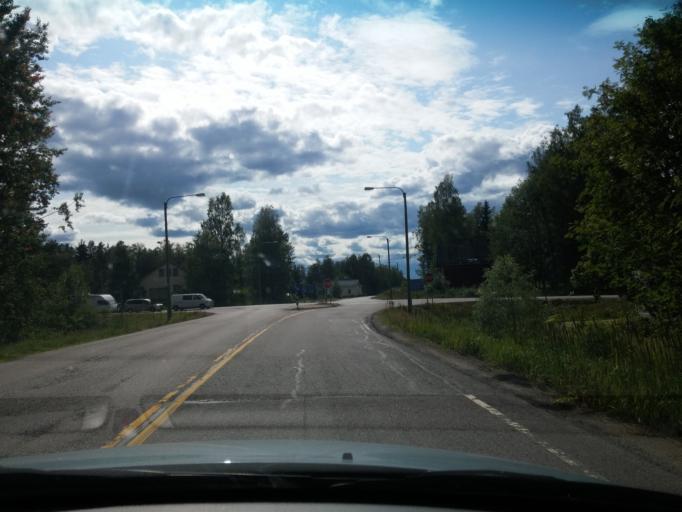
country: FI
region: Central Finland
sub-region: Saarijaervi-Viitasaari
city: Pylkoenmaeki
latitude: 62.5896
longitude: 24.5942
